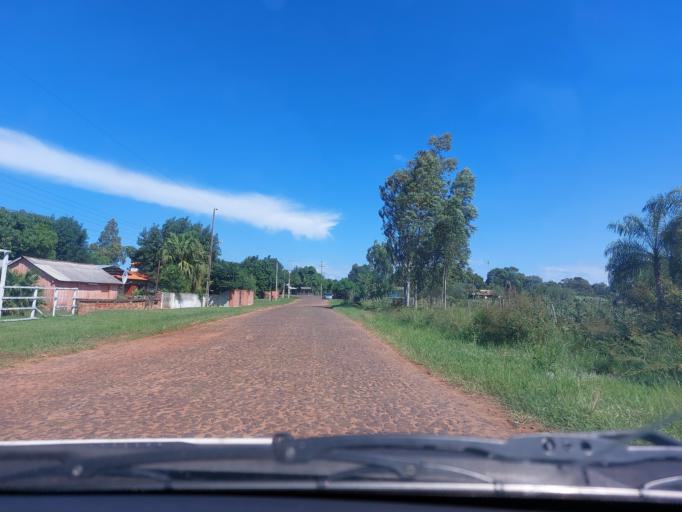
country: PY
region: San Pedro
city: Itacurubi del Rosario
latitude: -24.5907
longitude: -56.6028
